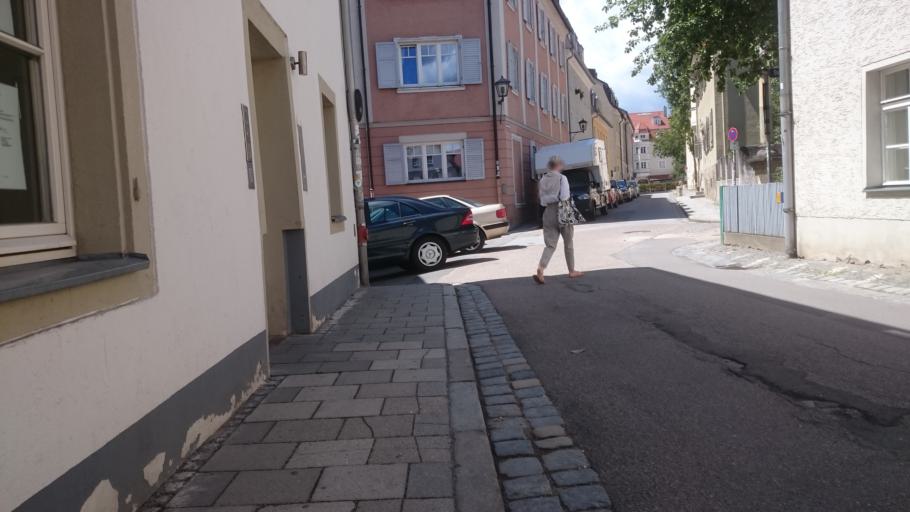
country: DE
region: Bavaria
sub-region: Upper Palatinate
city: Regensburg
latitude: 49.0243
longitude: 12.0999
